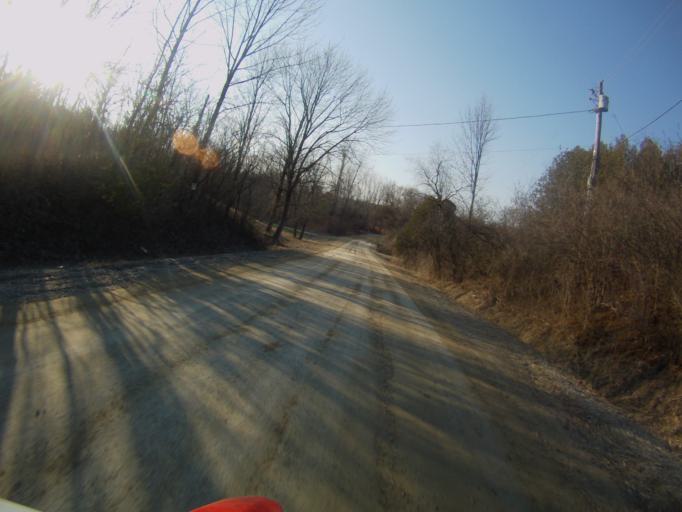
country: US
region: Vermont
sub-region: Addison County
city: Middlebury (village)
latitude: 44.0581
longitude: -73.1465
